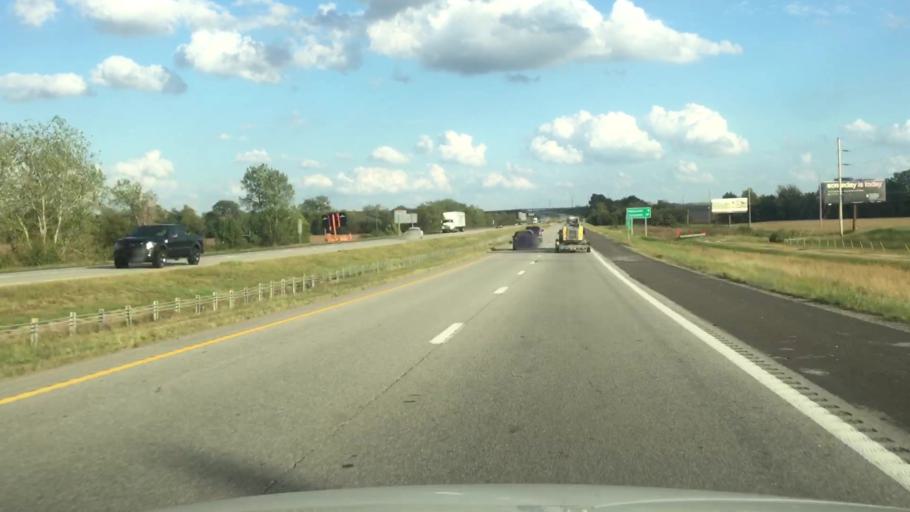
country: US
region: Missouri
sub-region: Lafayette County
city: Higginsville
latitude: 38.9980
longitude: -93.7227
